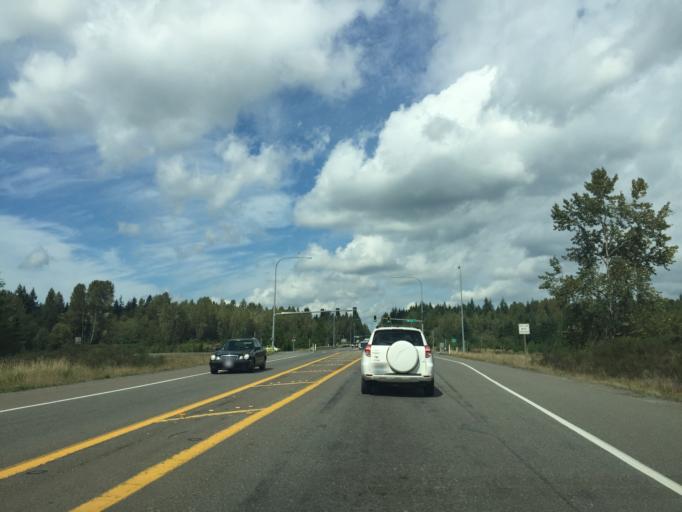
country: US
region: Washington
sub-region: Snohomish County
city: Fobes Hill
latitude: 47.9496
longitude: -122.1013
